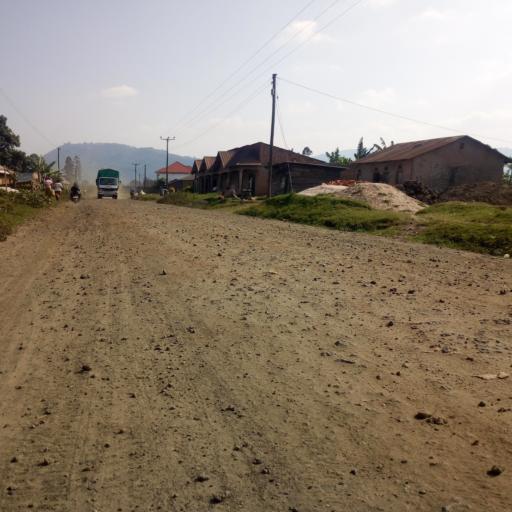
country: UG
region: Western Region
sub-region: Kisoro District
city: Kisoro
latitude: -1.2370
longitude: 29.7131
